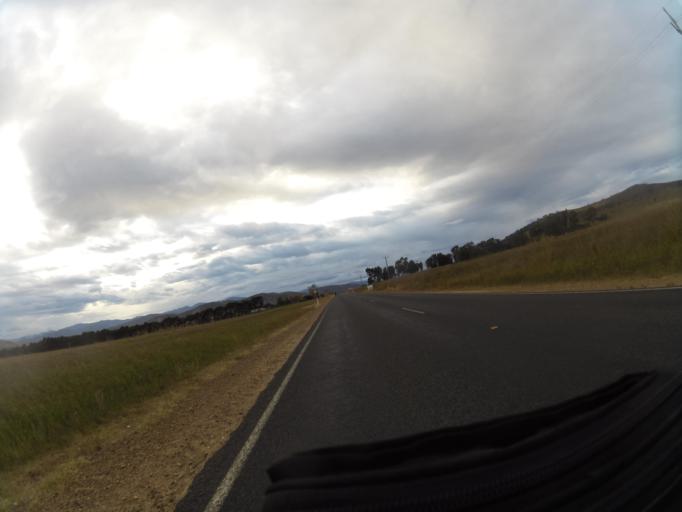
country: AU
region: New South Wales
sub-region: Greater Hume Shire
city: Holbrook
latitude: -36.0703
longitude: 147.9611
